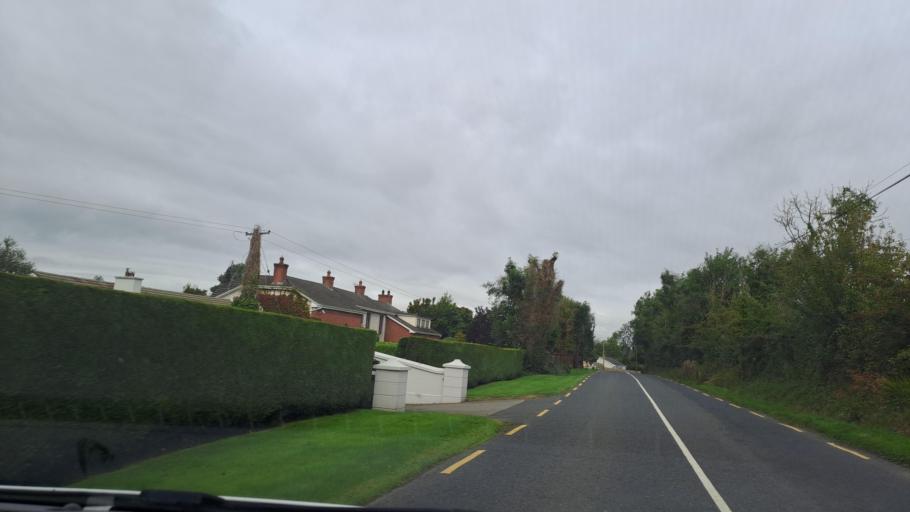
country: IE
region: Ulster
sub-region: An Cabhan
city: Kingscourt
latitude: 53.8874
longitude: -6.7495
